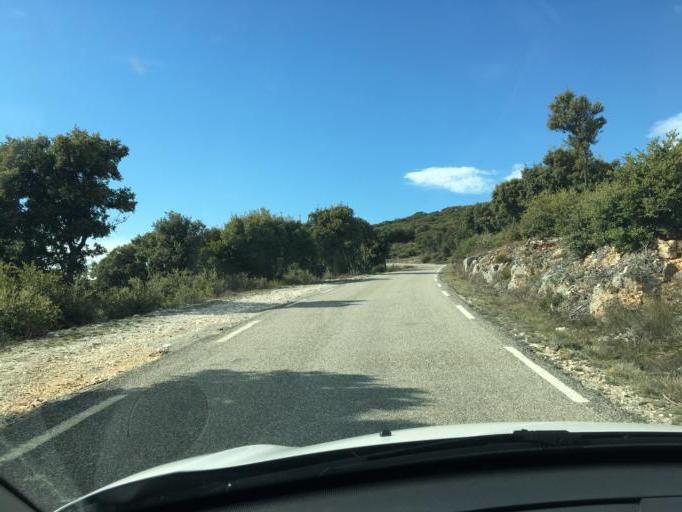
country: FR
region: Provence-Alpes-Cote d'Azur
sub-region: Departement du Vaucluse
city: Saint-Saturnin-les-Apt
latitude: 43.9552
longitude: 5.4644
